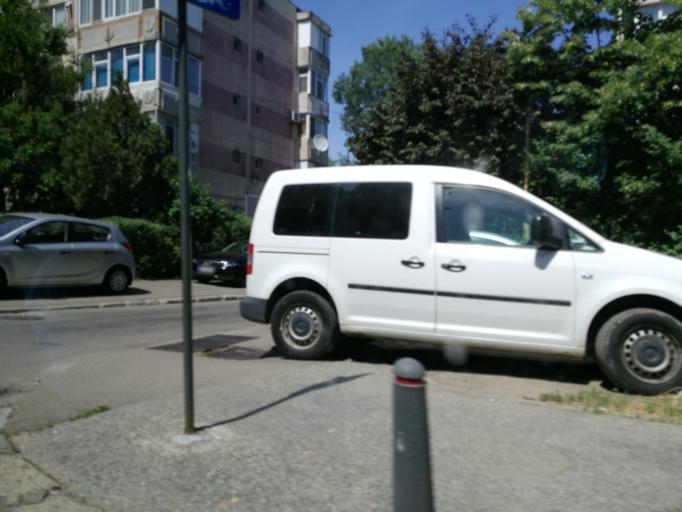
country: RO
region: Constanta
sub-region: Municipiul Constanta
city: Constanta
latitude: 44.2030
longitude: 28.6272
